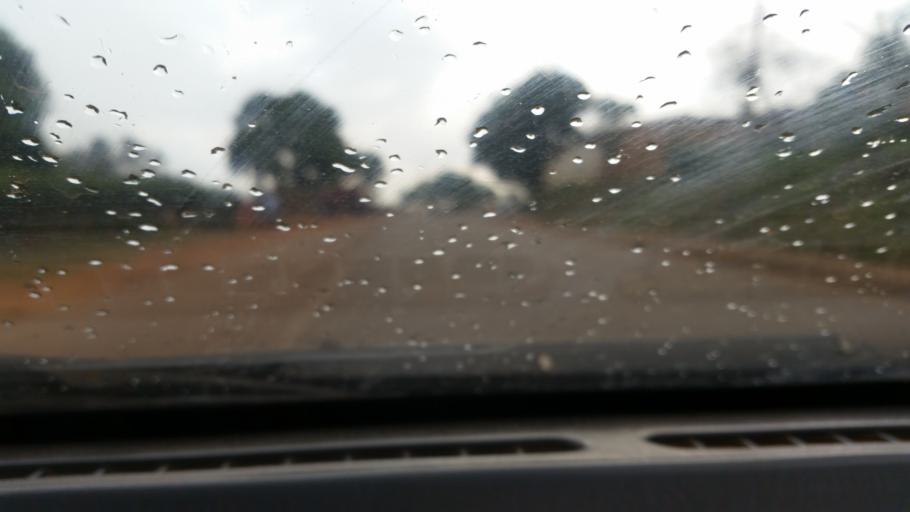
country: UG
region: Central Region
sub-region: Wakiso District
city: Kireka
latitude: 0.3514
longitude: 32.6512
